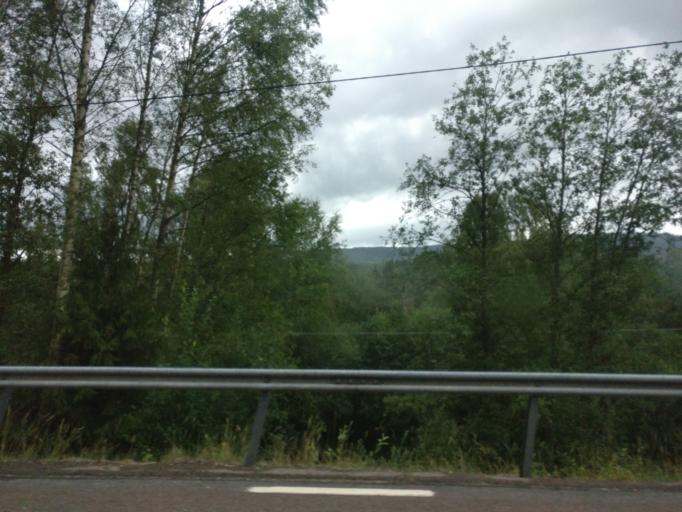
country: SE
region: Vaermland
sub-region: Torsby Kommun
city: Torsby
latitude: 60.6415
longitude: 13.0074
